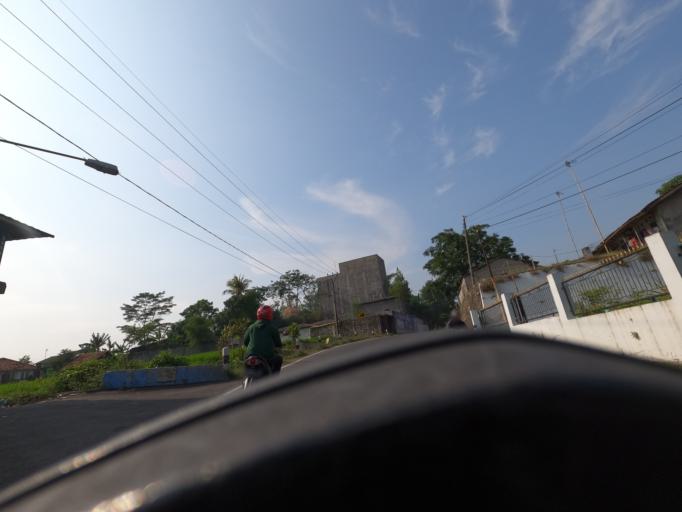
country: ID
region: West Java
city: Lembang
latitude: -6.6178
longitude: 107.7278
